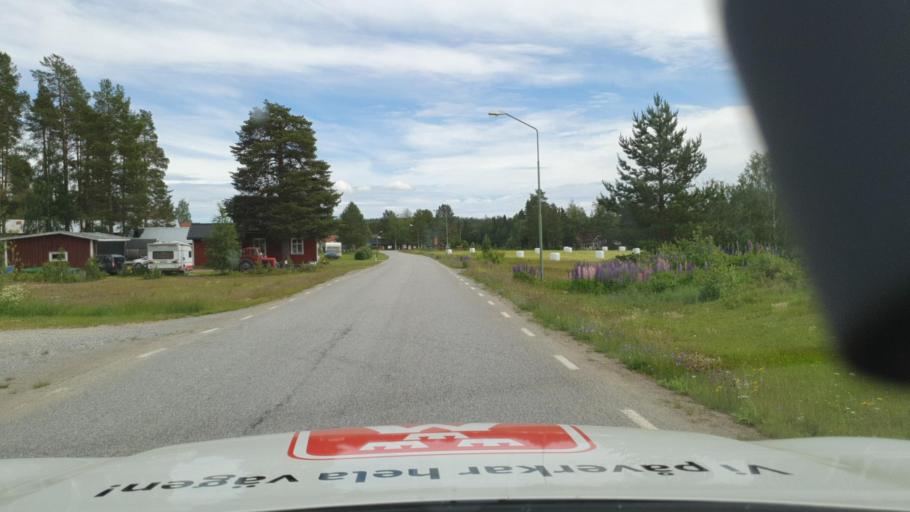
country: SE
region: Vaesterbotten
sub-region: Skelleftea Kommun
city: Burtraesk
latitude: 64.4987
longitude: 20.8539
